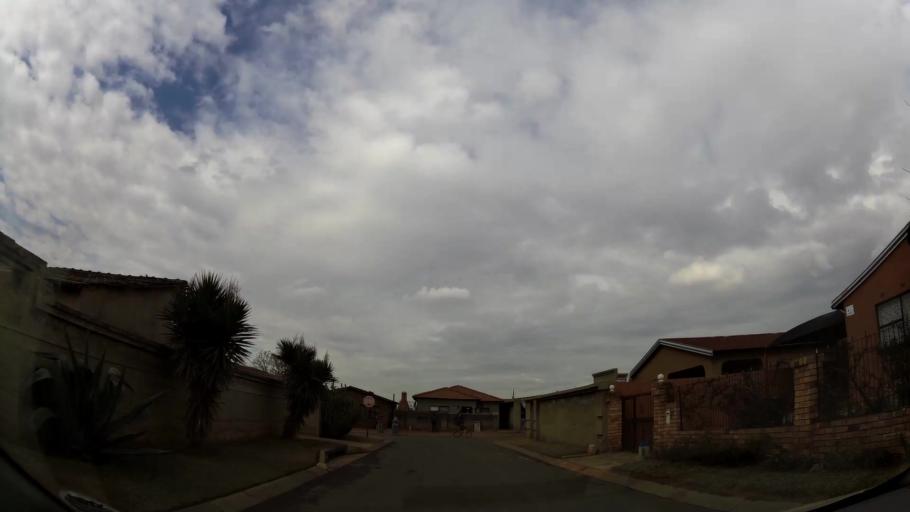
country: ZA
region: Gauteng
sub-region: Ekurhuleni Metropolitan Municipality
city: Germiston
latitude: -26.3838
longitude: 28.1671
